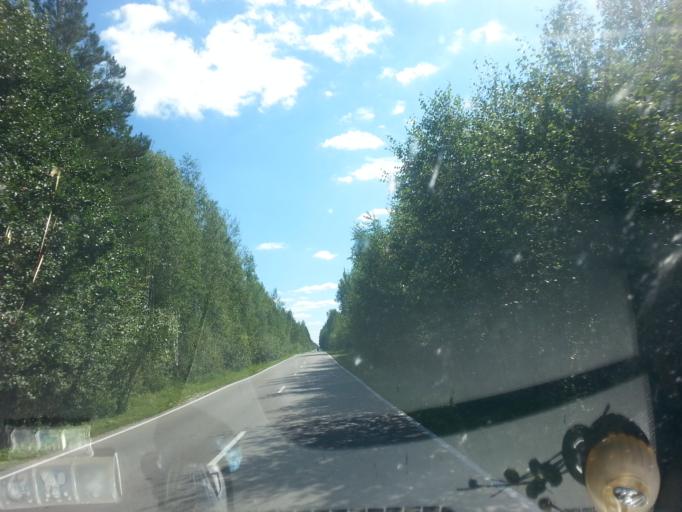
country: RU
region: Vladimir
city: Galitsy
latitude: 56.1270
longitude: 42.8735
